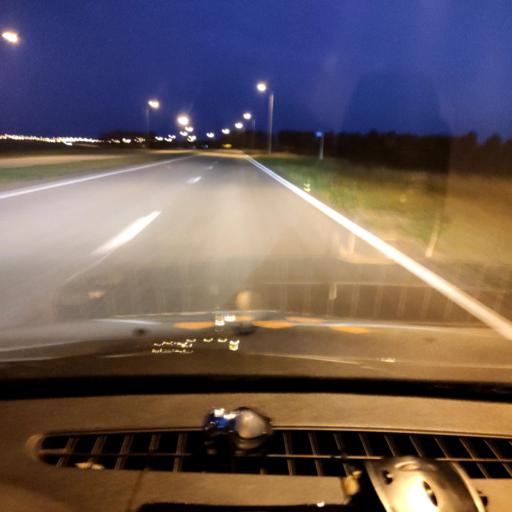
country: RU
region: Belgorod
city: Skorodnoye
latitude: 51.0771
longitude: 37.2087
